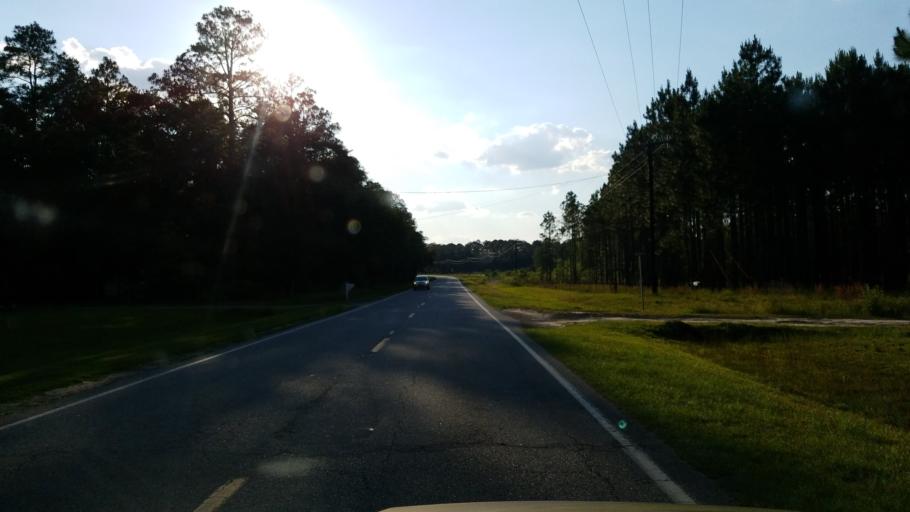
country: US
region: Georgia
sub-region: Berrien County
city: Nashville
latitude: 31.1935
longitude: -83.2118
